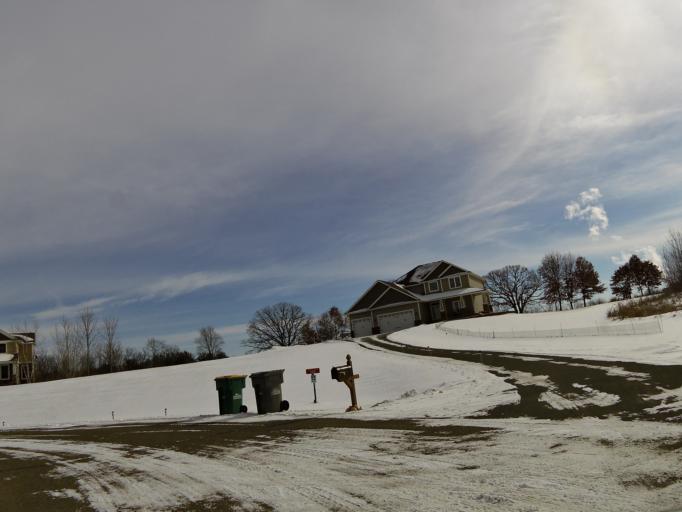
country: US
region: Minnesota
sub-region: Washington County
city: Stillwater
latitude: 45.0652
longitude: -92.7701
